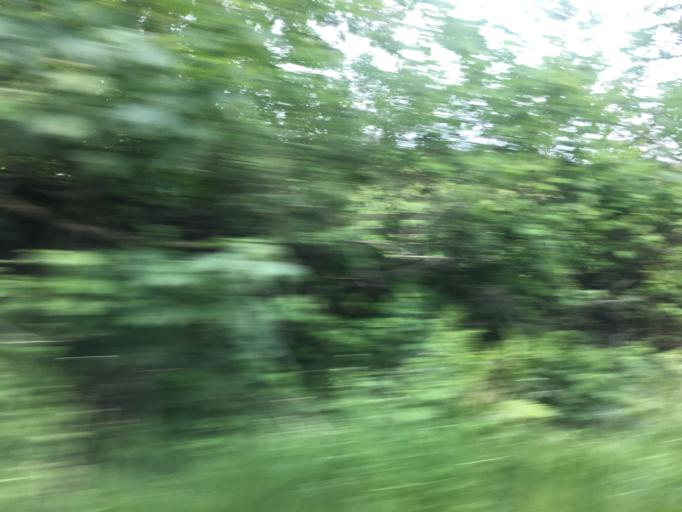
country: GB
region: Wales
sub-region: County of Ceredigion
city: Lampeter
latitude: 52.0850
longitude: -4.0491
